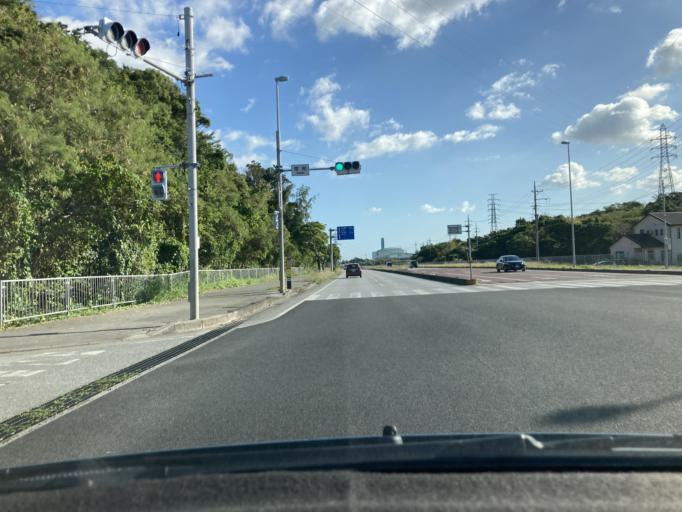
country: JP
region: Okinawa
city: Ishikawa
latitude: 26.4088
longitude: 127.8203
